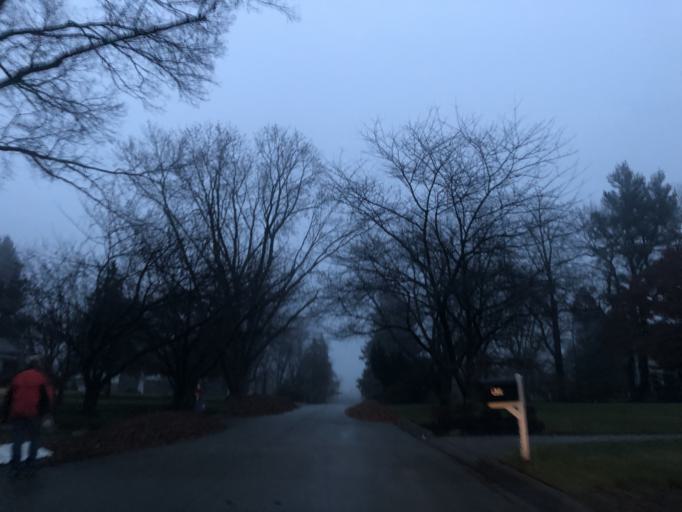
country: US
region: Pennsylvania
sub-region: Delaware County
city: Radnor
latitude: 40.0244
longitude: -75.3555
